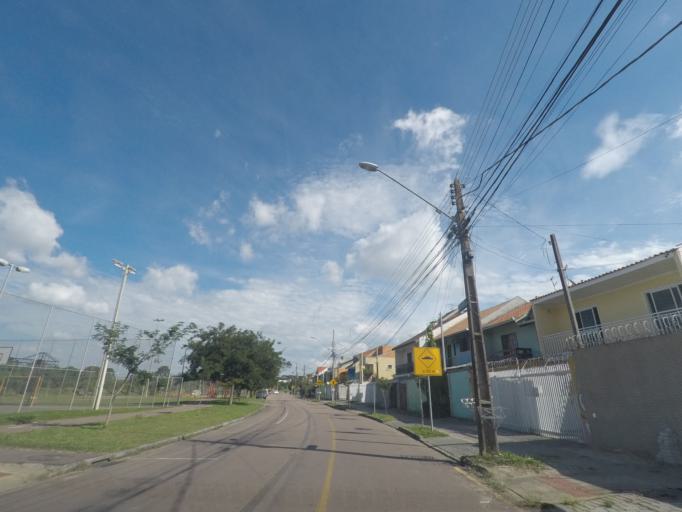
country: BR
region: Parana
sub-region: Curitiba
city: Curitiba
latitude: -25.4787
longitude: -49.3349
